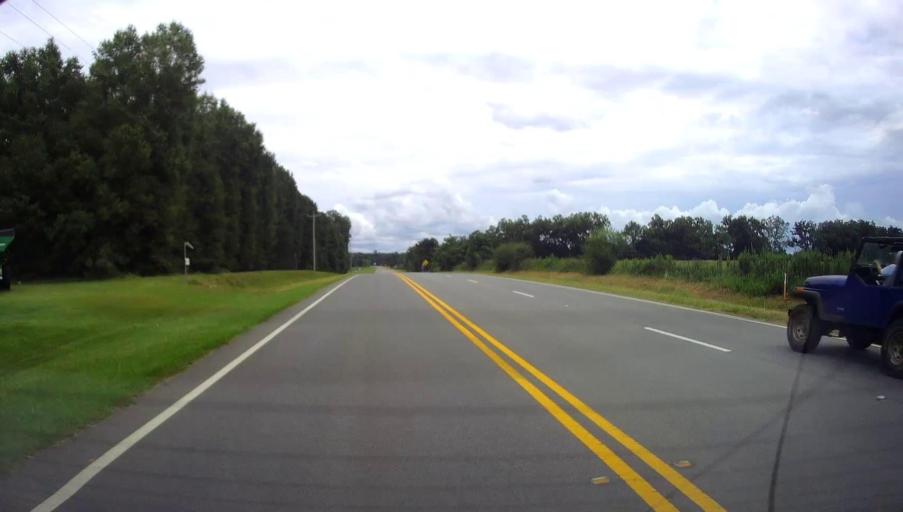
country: US
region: Georgia
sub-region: Macon County
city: Montezuma
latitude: 32.2920
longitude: -83.9295
